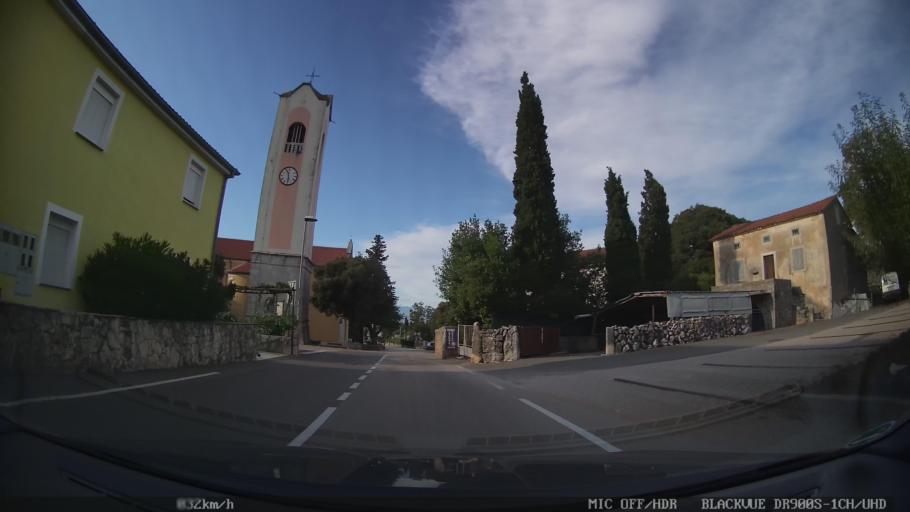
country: HR
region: Primorsko-Goranska
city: Njivice
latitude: 45.1175
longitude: 14.5270
